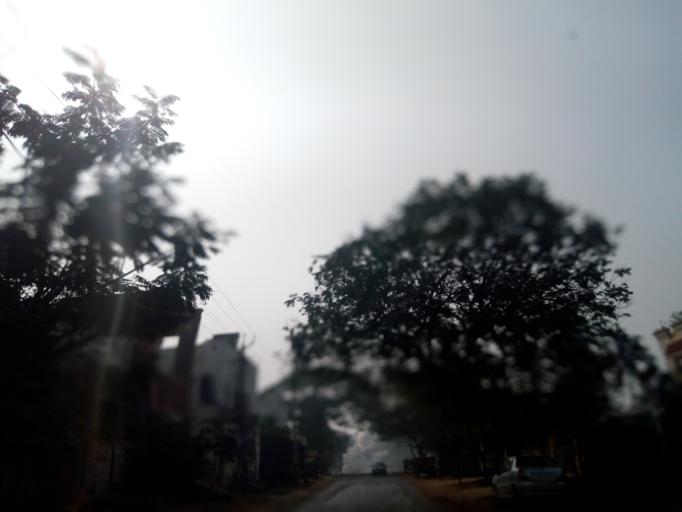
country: IN
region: Andhra Pradesh
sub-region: West Godavari
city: Tadepallegudem
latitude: 16.8172
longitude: 81.4061
